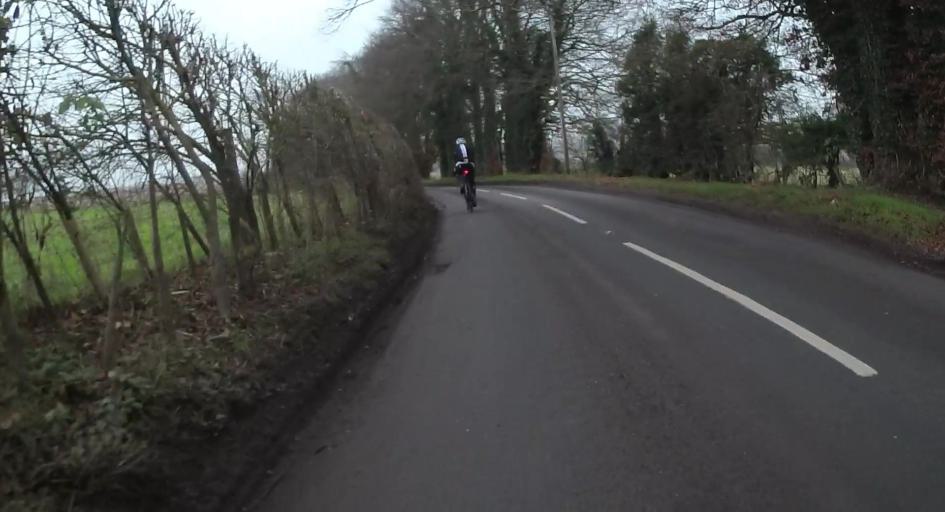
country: GB
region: England
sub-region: Hampshire
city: Overton
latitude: 51.1460
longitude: -1.1801
